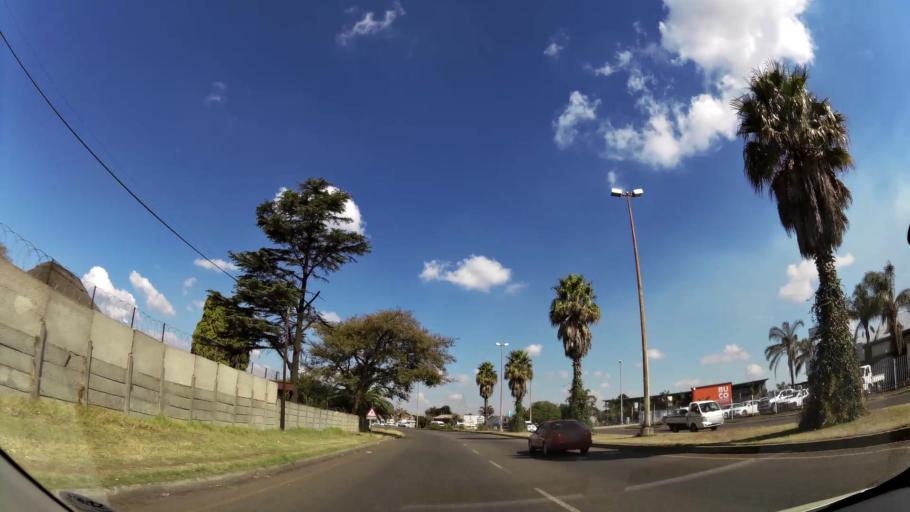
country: ZA
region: Mpumalanga
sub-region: Nkangala District Municipality
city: Witbank
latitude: -25.8947
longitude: 29.2300
